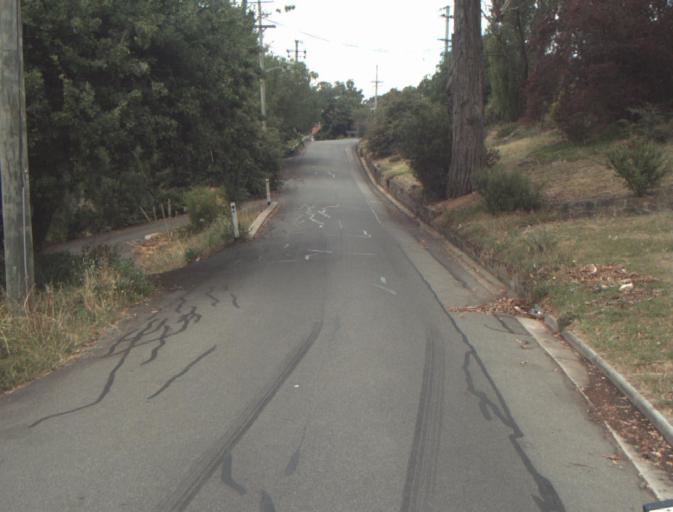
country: AU
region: Tasmania
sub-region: Launceston
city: Launceston
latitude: -41.4382
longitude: 147.1249
